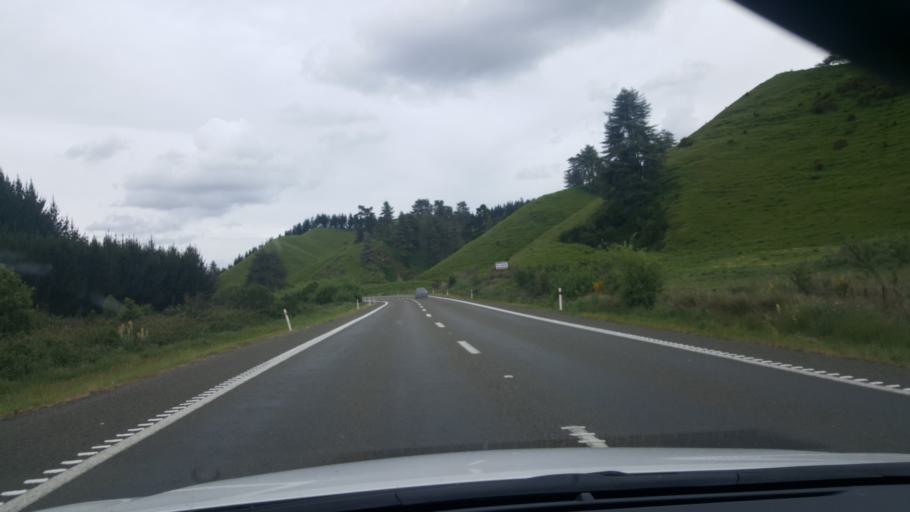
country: NZ
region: Bay of Plenty
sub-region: Rotorua District
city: Rotorua
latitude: -38.2196
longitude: 176.2818
